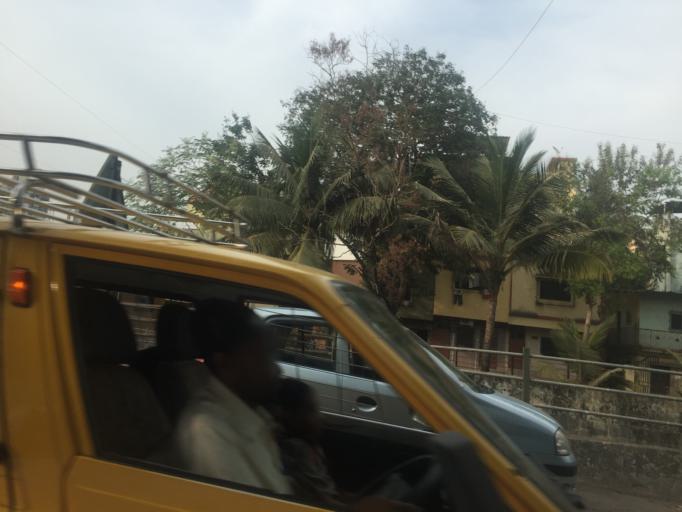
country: IN
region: Maharashtra
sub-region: Thane
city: Airoli
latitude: 19.1556
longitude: 72.9958
